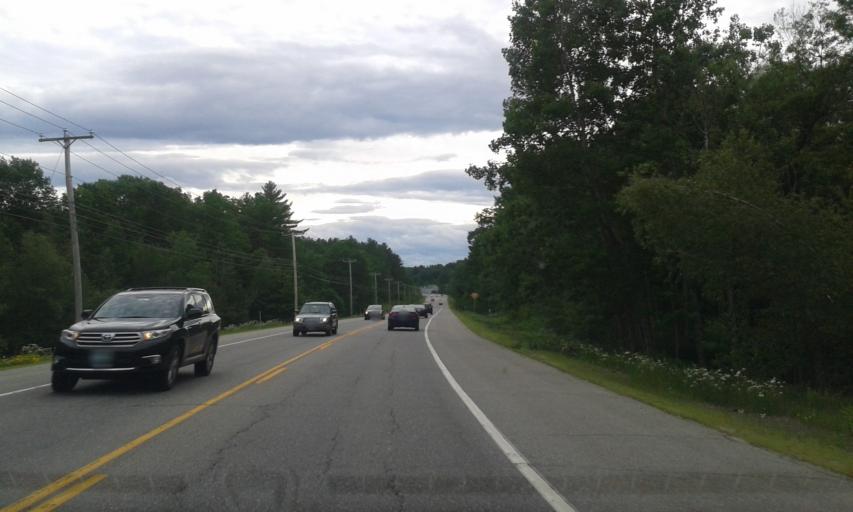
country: US
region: New Hampshire
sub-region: Hillsborough County
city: Litchfield
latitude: 42.8071
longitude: -71.5322
